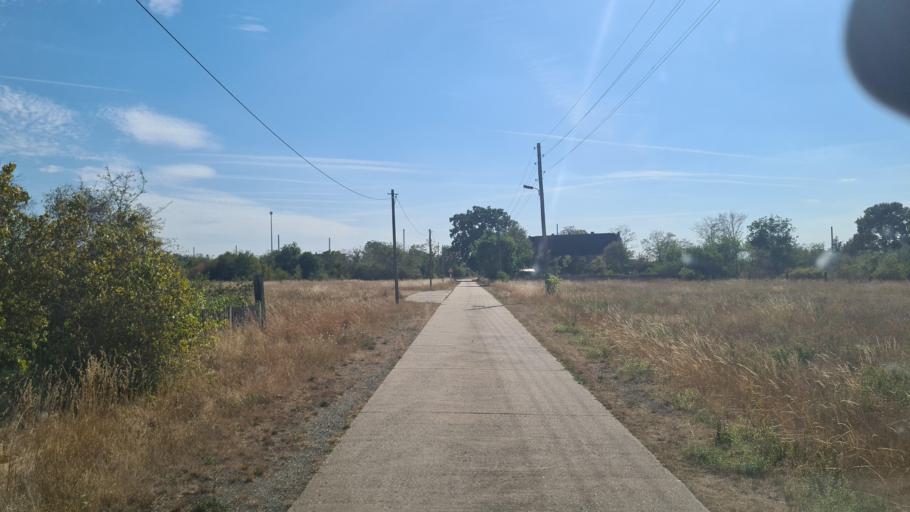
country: DE
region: Saxony
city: Zeithain
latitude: 51.3795
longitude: 13.3148
